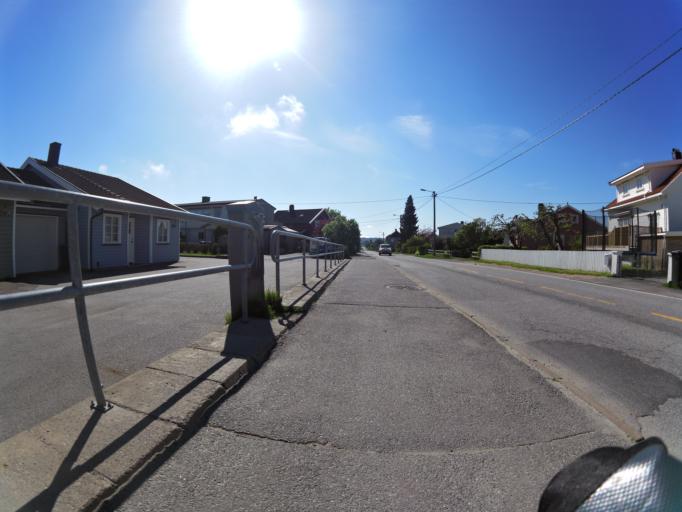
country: NO
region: Ostfold
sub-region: Fredrikstad
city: Fredrikstad
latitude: 59.2318
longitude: 11.0062
